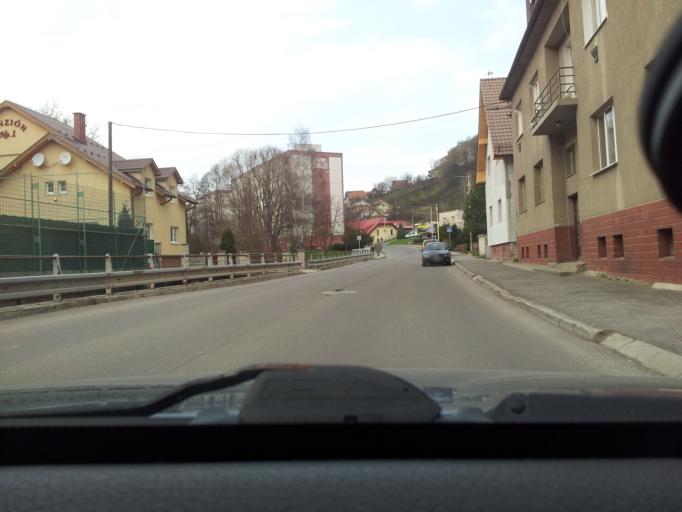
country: SK
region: Banskobystricky
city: Nova Bana
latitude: 48.4229
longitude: 18.6423
